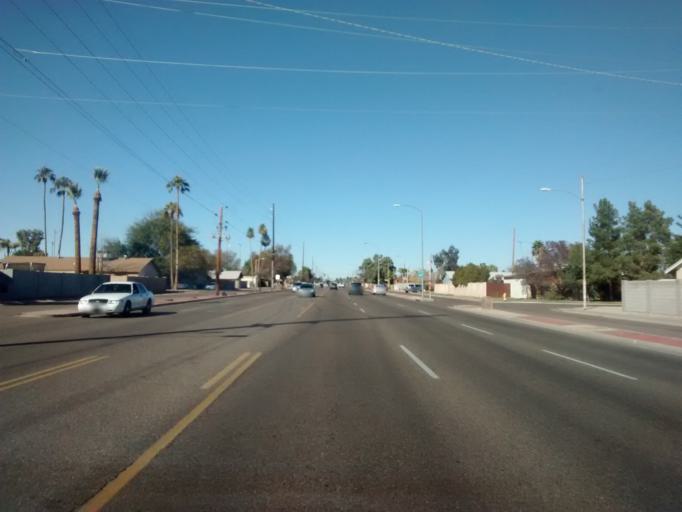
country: US
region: Arizona
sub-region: Maricopa County
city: Glendale
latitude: 33.5901
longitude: -112.1340
